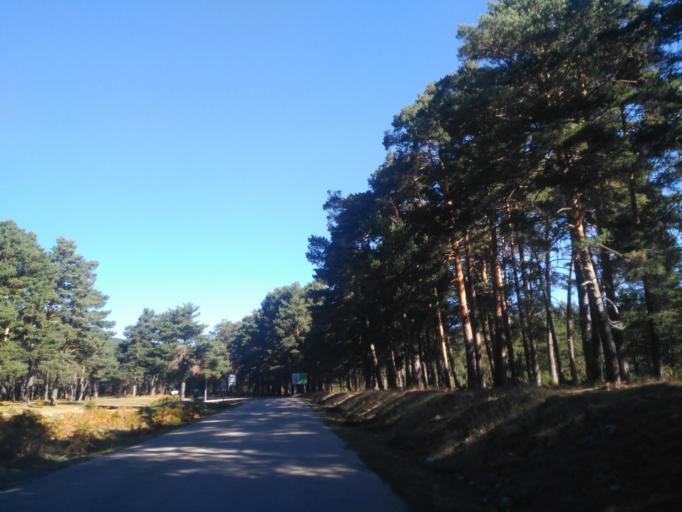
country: ES
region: Castille and Leon
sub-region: Provincia de Soria
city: Vinuesa
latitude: 41.9962
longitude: -2.7998
